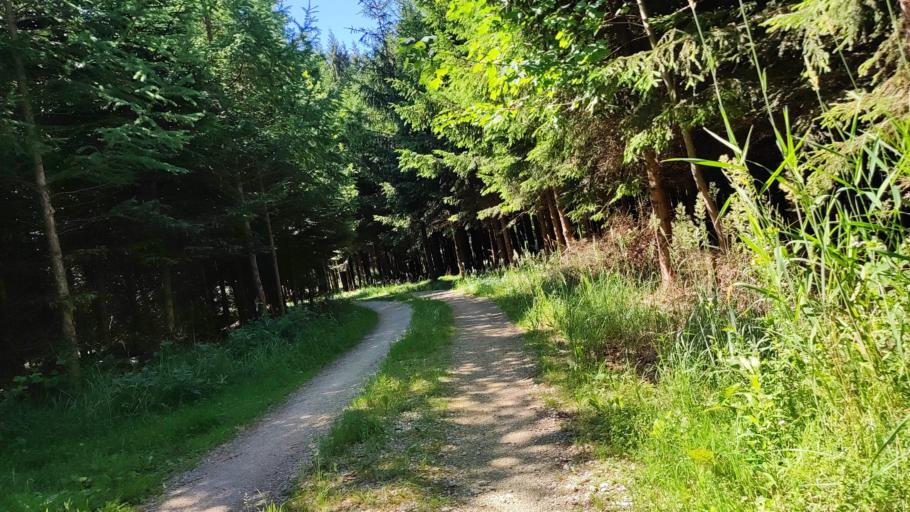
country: DE
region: Bavaria
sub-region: Swabia
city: Landensberg
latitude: 48.4613
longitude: 10.5291
